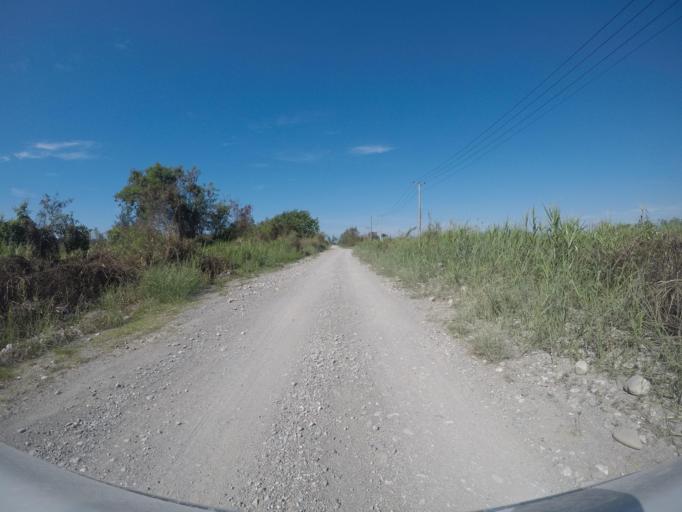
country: TL
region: Viqueque
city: Viqueque
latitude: -8.9419
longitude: 126.1137
